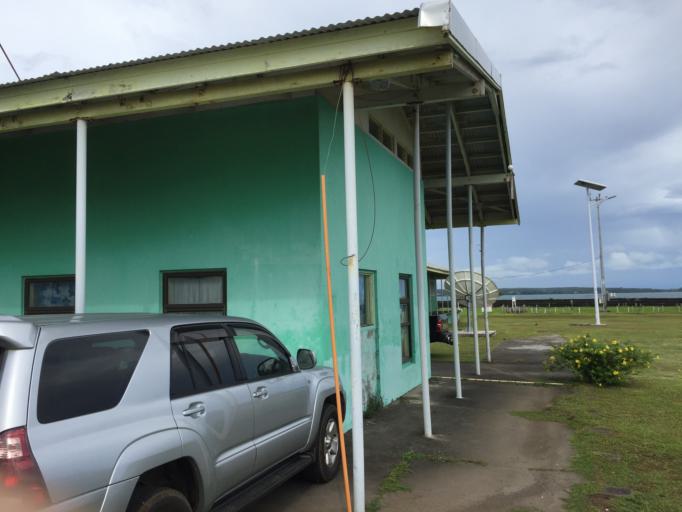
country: WS
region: Tuamasaga
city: Vaiusu
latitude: -13.8149
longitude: -171.7803
